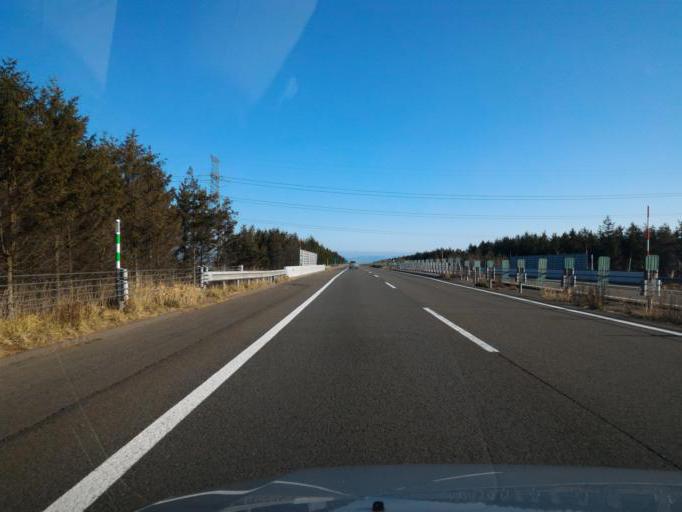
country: JP
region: Hokkaido
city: Ebetsu
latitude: 43.1192
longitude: 141.6273
